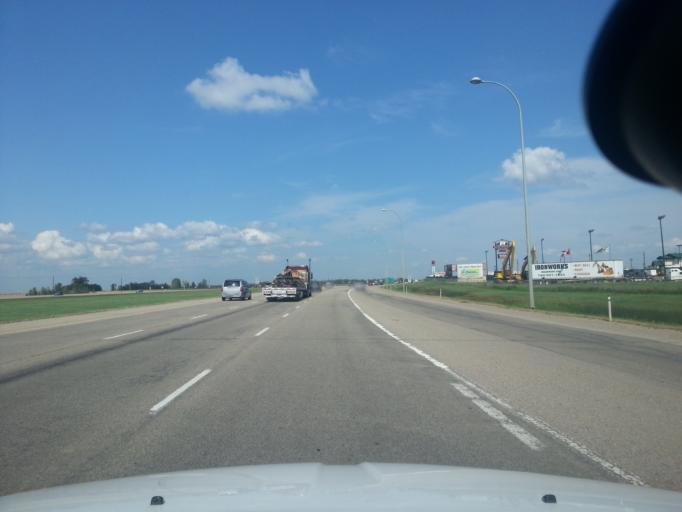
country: CA
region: Alberta
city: Leduc
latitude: 53.3402
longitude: -113.5475
